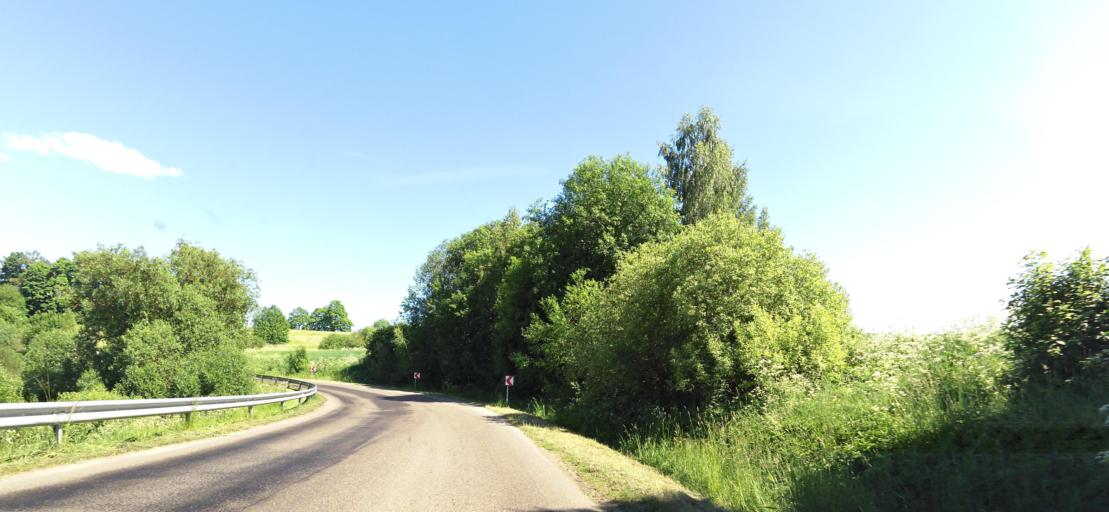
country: LT
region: Utenos apskritis
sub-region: Anyksciai
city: Anyksciai
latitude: 55.3201
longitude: 25.1264
